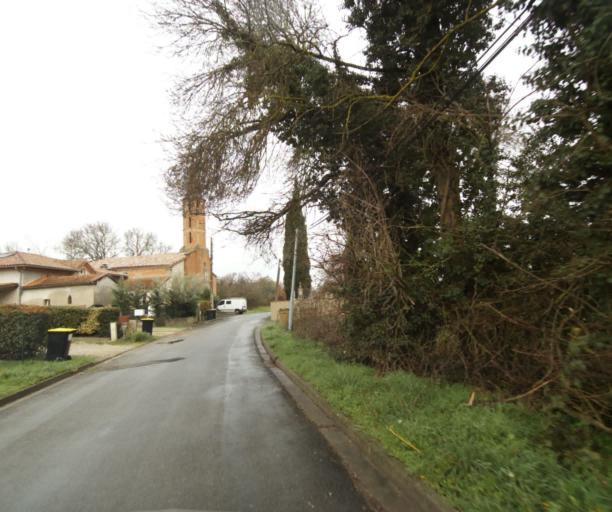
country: FR
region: Midi-Pyrenees
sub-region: Departement du Tarn-et-Garonne
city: Nohic
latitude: 43.8716
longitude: 1.4674
